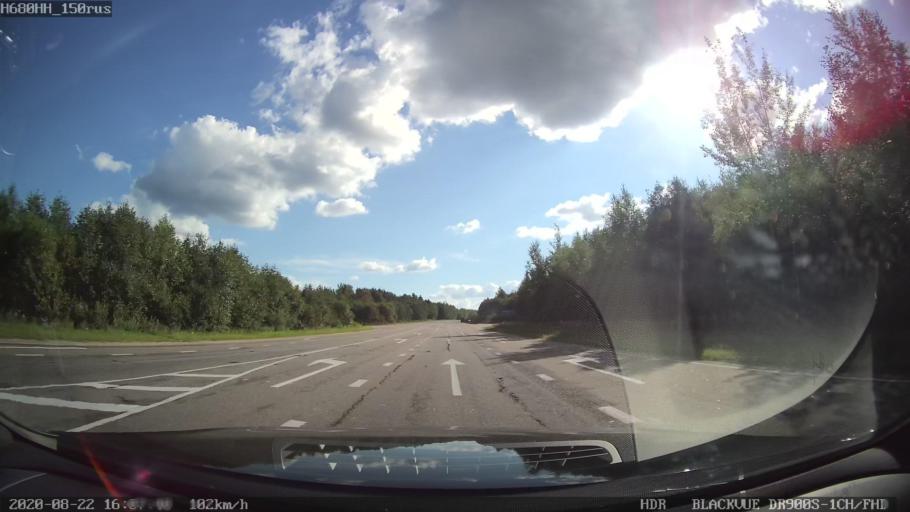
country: RU
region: Tverskaya
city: Rameshki
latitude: 57.5496
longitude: 36.3103
